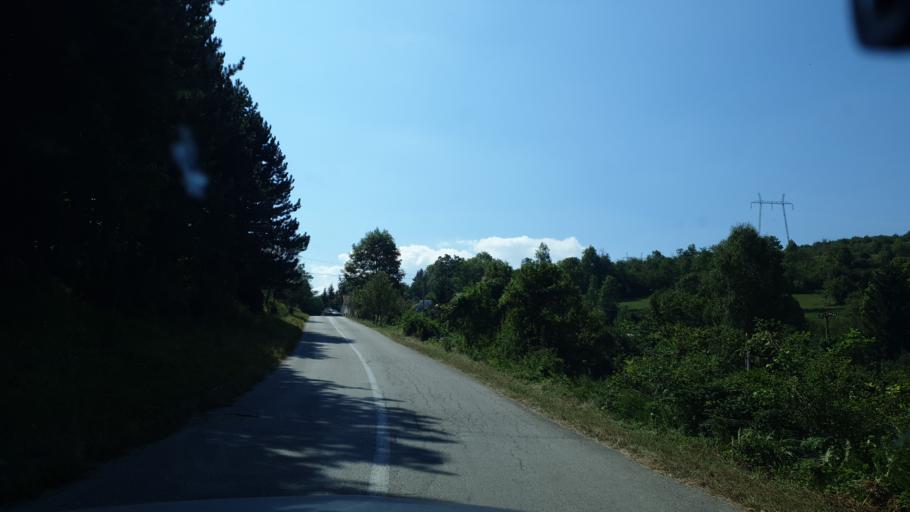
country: RS
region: Central Serbia
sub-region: Zlatiborski Okrug
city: Cajetina
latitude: 43.6926
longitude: 19.8483
